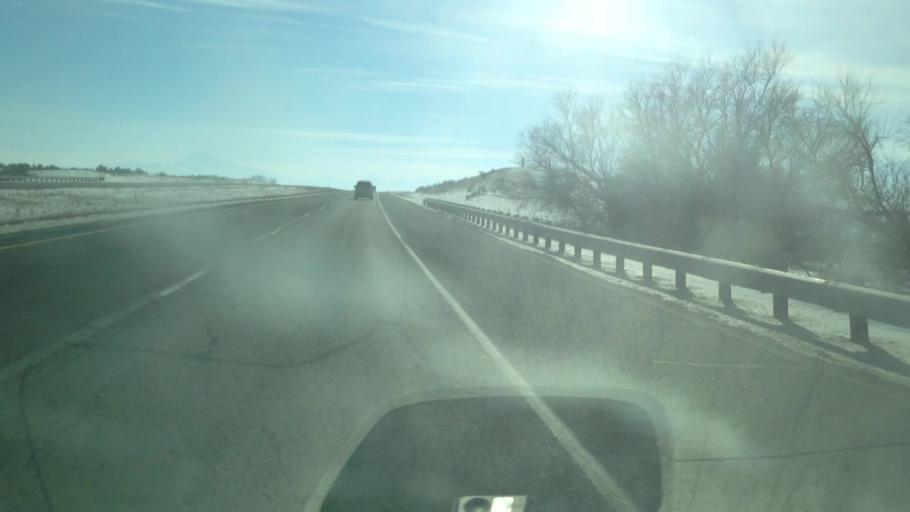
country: US
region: Idaho
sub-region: Oneida County
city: Malad City
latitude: 42.5392
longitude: -112.1719
